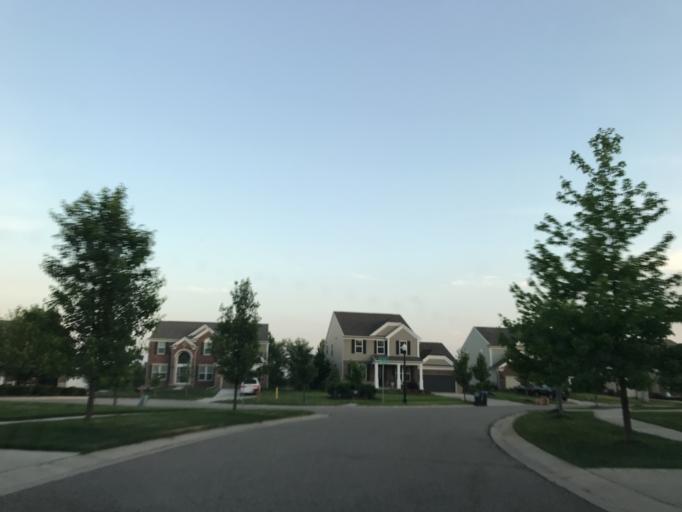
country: US
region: Michigan
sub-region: Oakland County
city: South Lyon
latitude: 42.4650
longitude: -83.6328
